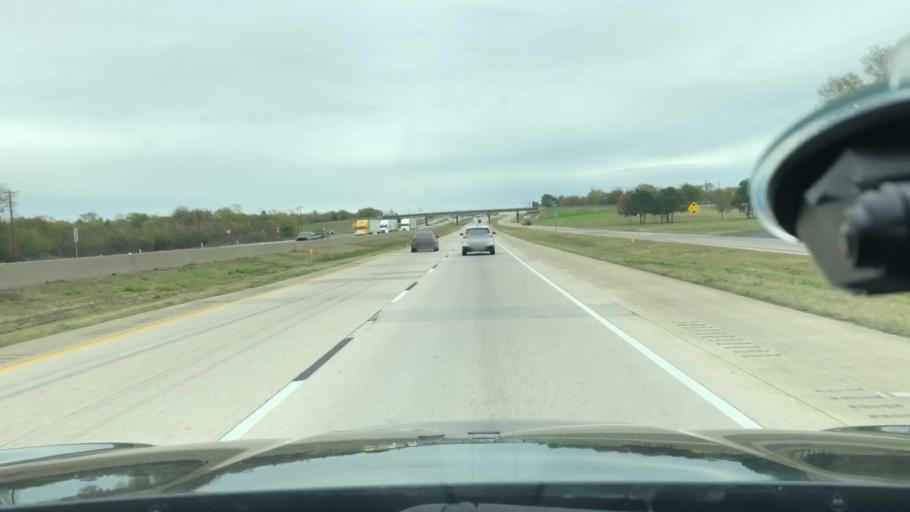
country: US
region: Texas
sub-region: Hopkins County
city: Sulphur Springs
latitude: 33.1210
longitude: -95.6763
